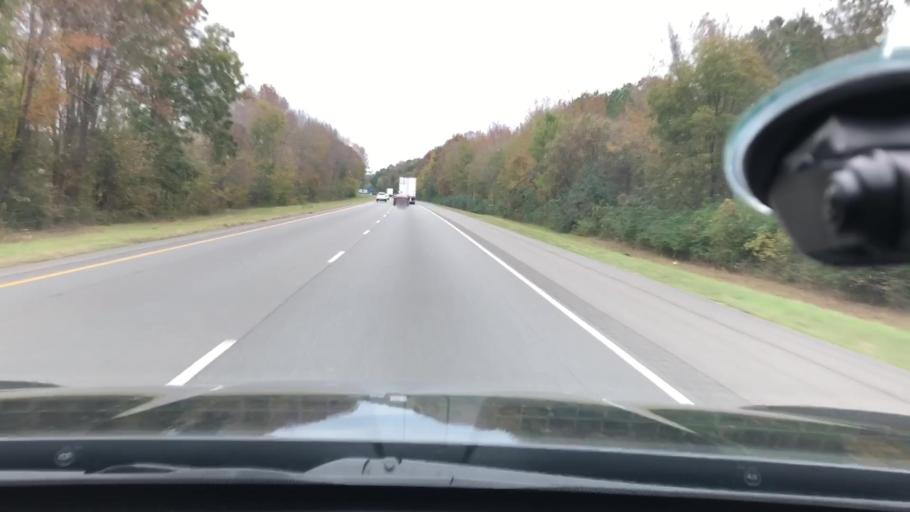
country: US
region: Arkansas
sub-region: Hempstead County
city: Hope
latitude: 33.6595
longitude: -93.6456
